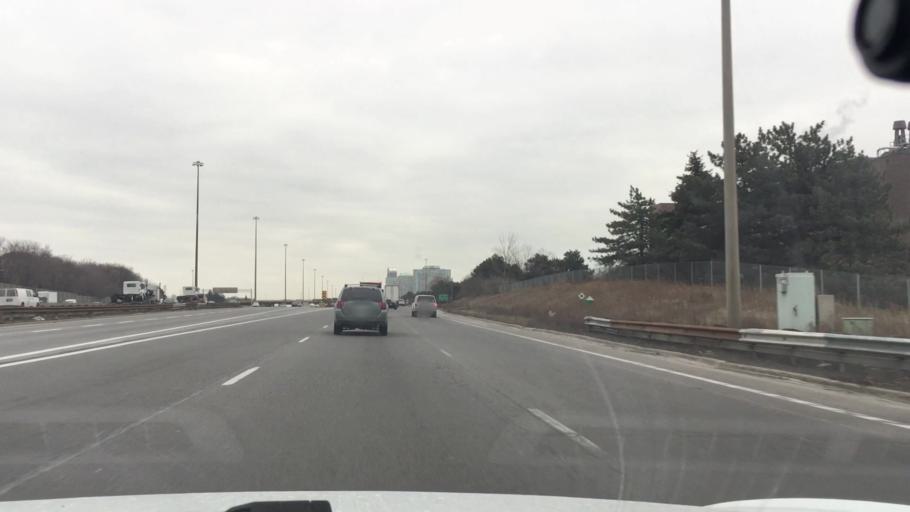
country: CA
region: Ontario
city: Scarborough
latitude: 43.7787
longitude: -79.2732
